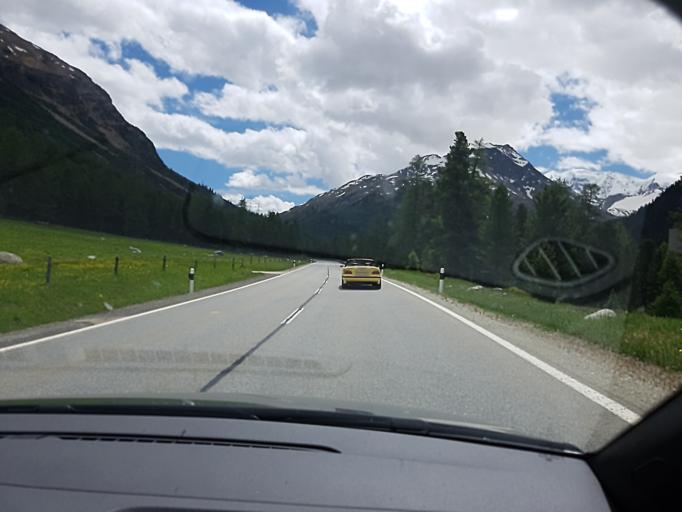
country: CH
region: Grisons
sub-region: Maloja District
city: Pontresina
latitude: 46.4681
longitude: 9.9292
